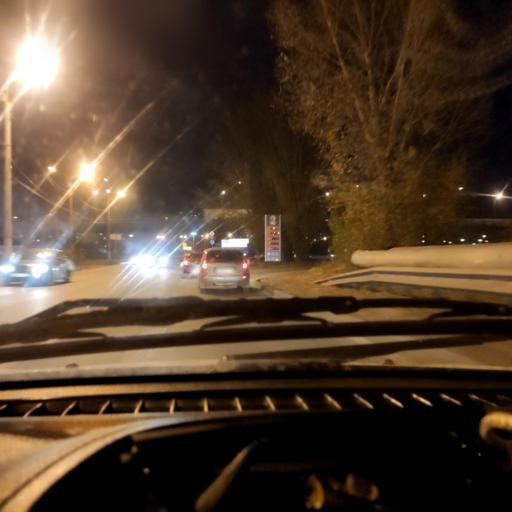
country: RU
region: Samara
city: Zhigulevsk
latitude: 53.4849
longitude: 49.5131
